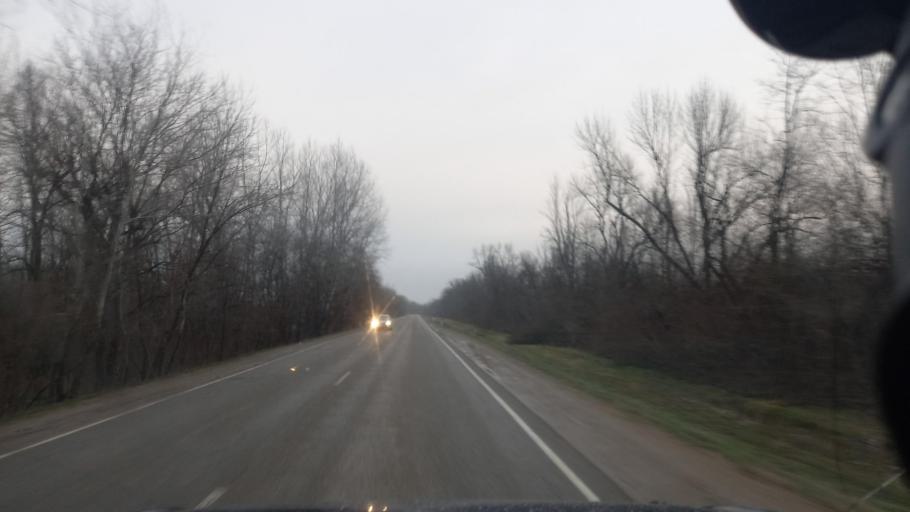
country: RU
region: Krasnodarskiy
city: Saratovskaya
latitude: 44.6855
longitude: 39.2140
